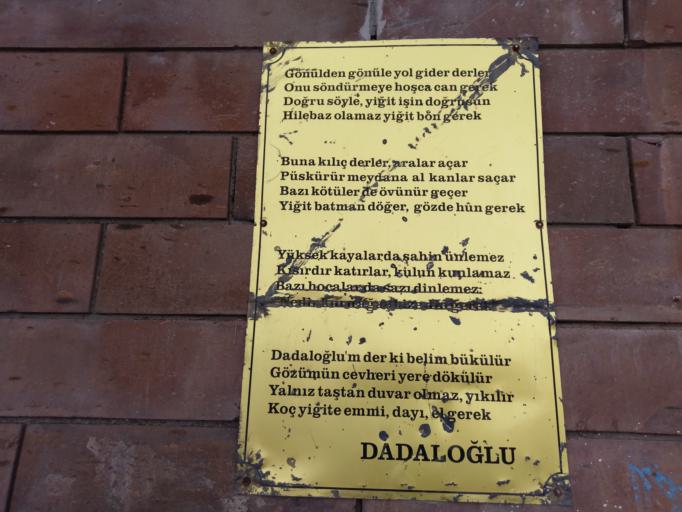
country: TR
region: Kayseri
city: Toklar
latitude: 38.5031
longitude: 36.1254
